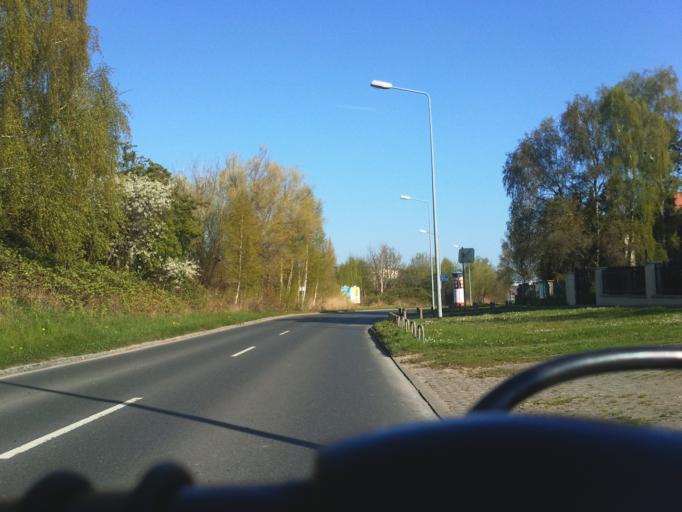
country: DE
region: Mecklenburg-Vorpommern
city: Rostock
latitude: 54.1031
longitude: 12.0924
